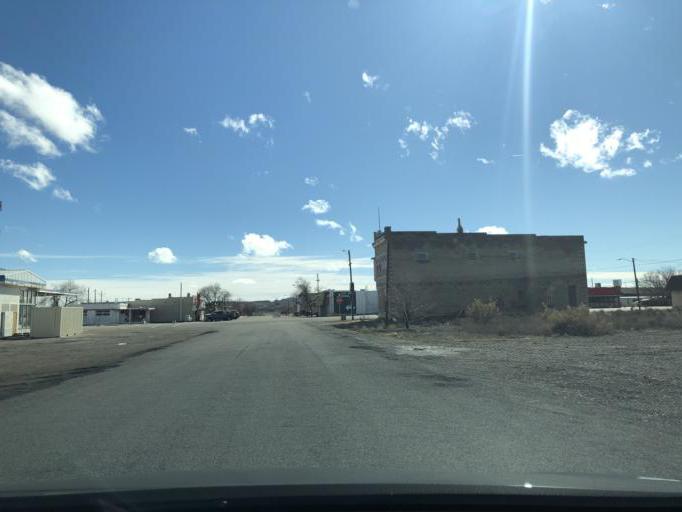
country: US
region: Utah
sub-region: Carbon County
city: East Carbon City
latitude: 38.9963
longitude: -110.1653
